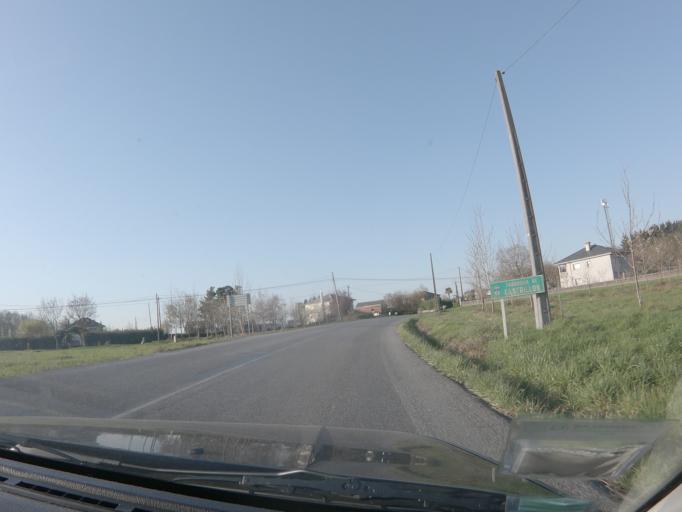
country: ES
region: Galicia
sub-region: Provincia de Lugo
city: Corgo
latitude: 42.9360
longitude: -7.3988
